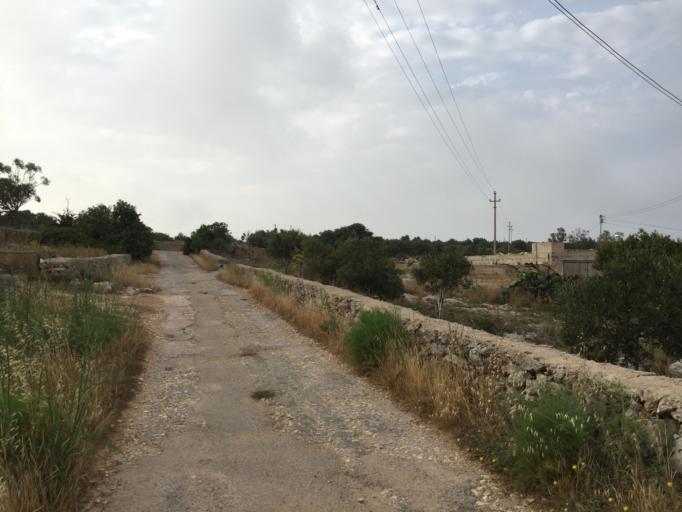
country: MT
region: L-Imgarr
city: Imgarr
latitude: 35.9332
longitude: 14.3861
